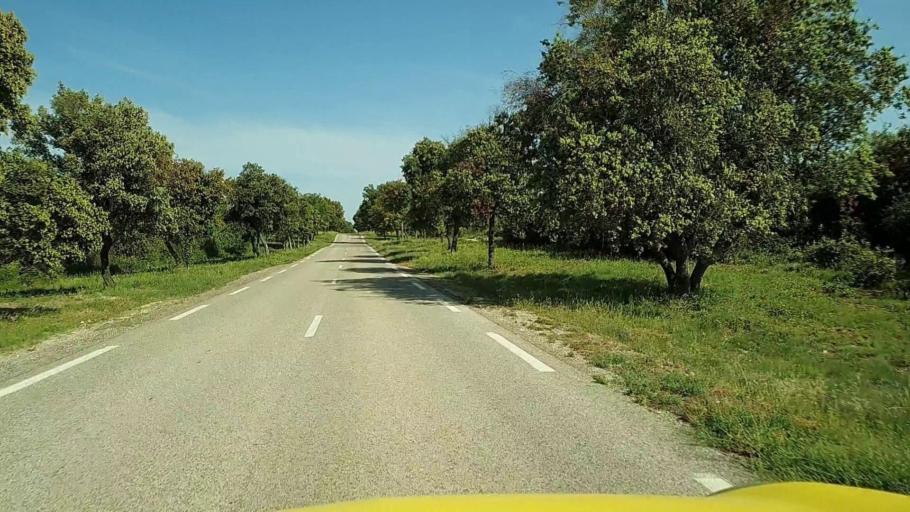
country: FR
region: Languedoc-Roussillon
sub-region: Departement du Gard
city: Montaren-et-Saint-Mediers
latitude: 44.1072
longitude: 4.3782
